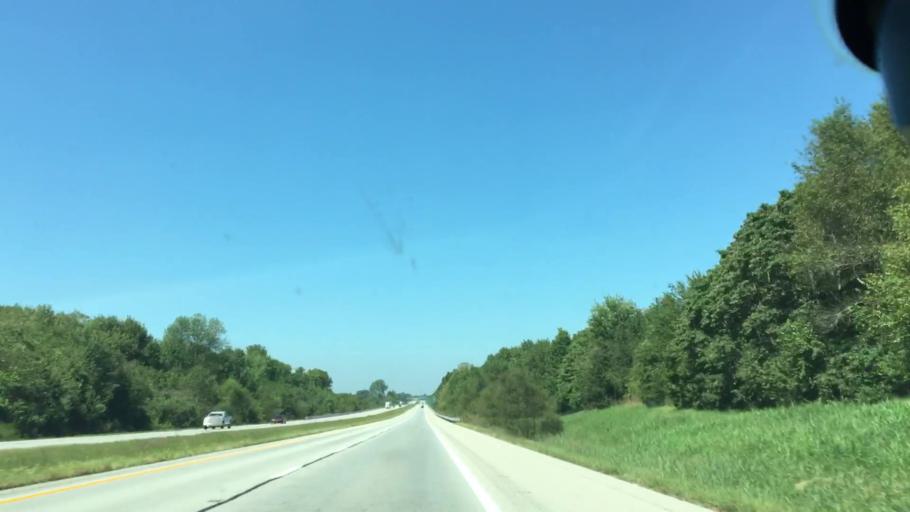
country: US
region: Kentucky
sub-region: Henderson County
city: Henderson
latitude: 37.7785
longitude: -87.5428
